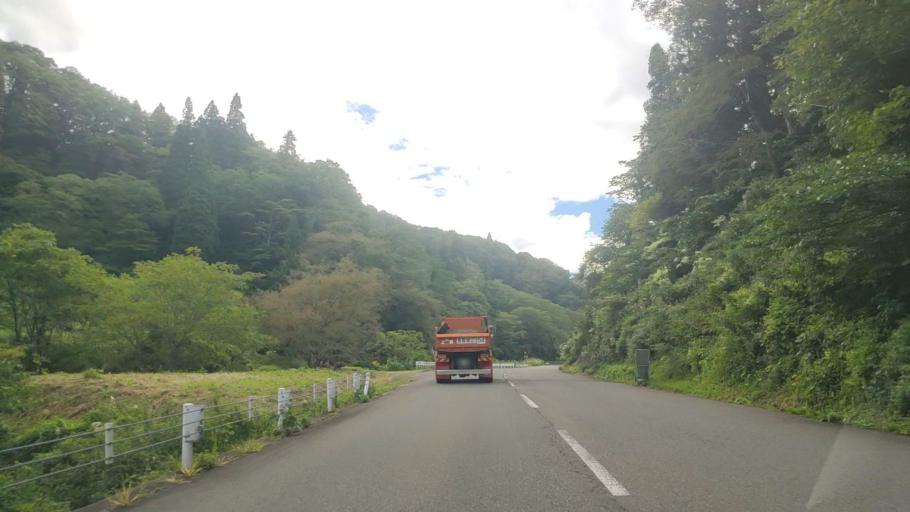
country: JP
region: Nagano
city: Iiyama
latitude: 36.8976
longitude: 138.3199
